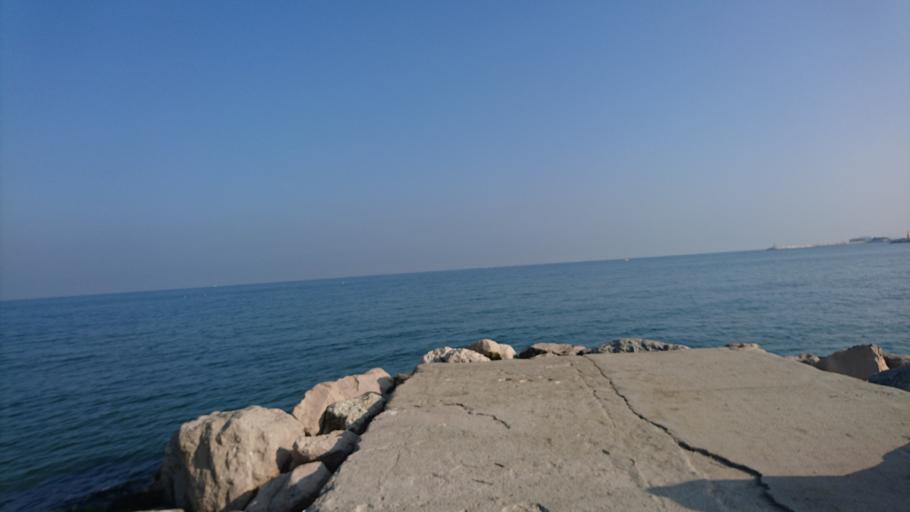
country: IT
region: Emilia-Romagna
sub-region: Provincia di Rimini
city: Rimini
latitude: 44.0770
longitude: 12.5650
